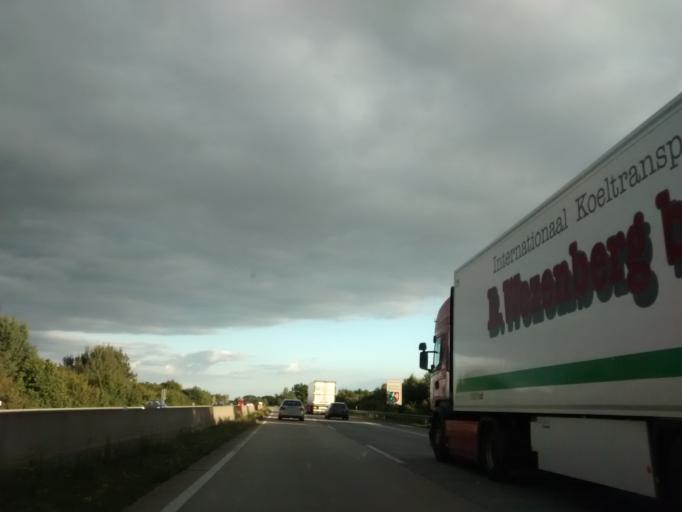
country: DE
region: North Rhine-Westphalia
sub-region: Regierungsbezirk Munster
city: Rheine
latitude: 52.3204
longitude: 7.4356
